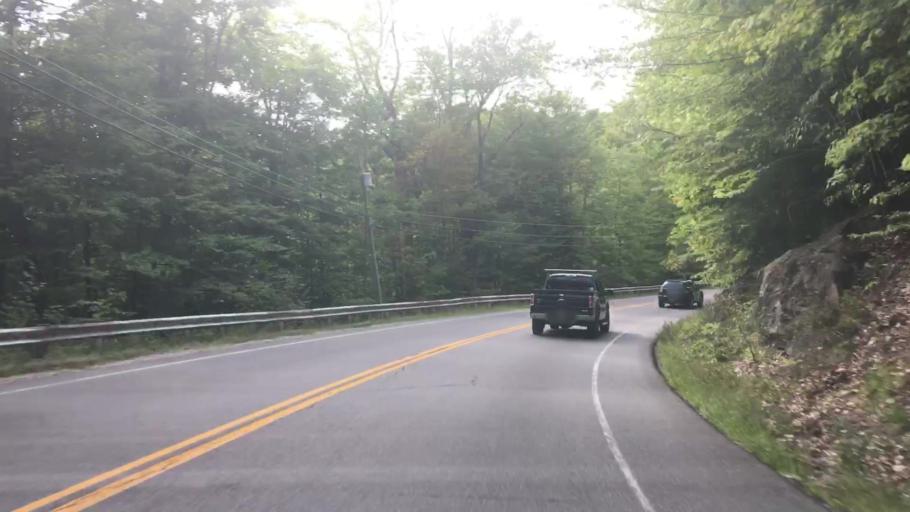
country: US
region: Maine
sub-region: Cumberland County
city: Raymond
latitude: 43.9849
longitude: -70.4921
